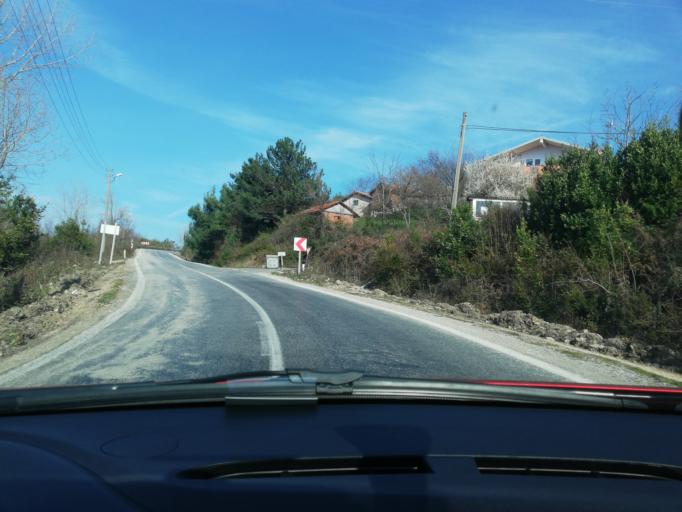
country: TR
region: Bartin
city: Kurucasile
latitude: 41.8460
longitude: 32.7401
